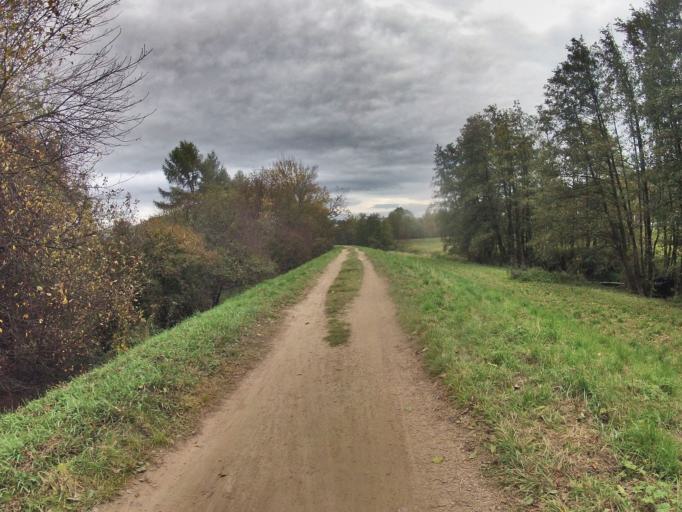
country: PL
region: Lesser Poland Voivodeship
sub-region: Krakow
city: Krakow
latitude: 50.0634
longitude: 19.8942
